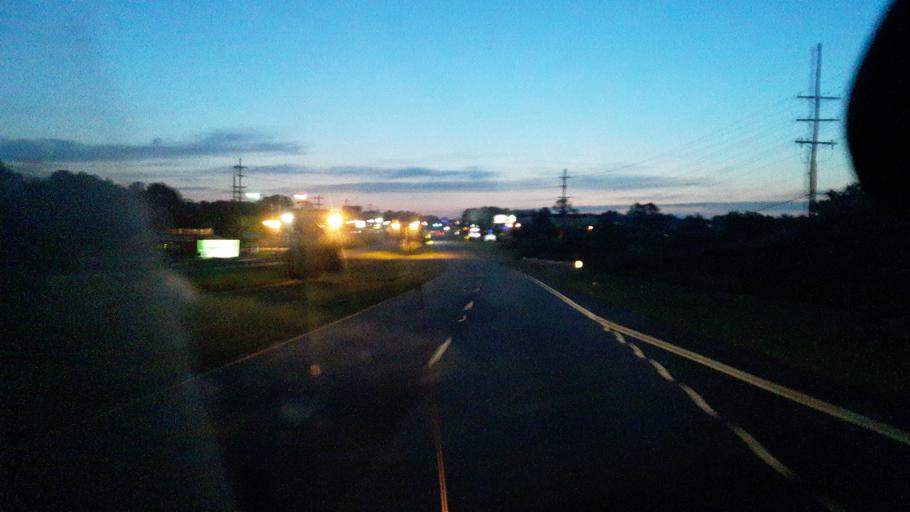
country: US
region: South Carolina
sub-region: Horry County
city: Little River
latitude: 33.8649
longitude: -78.6429
